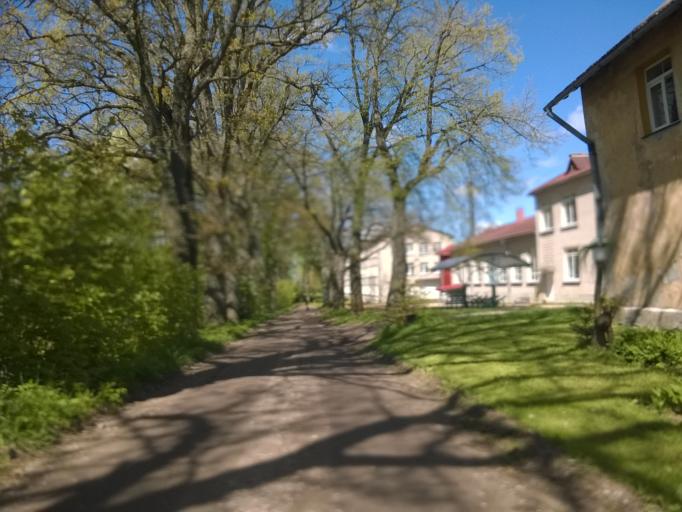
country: LV
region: Amatas Novads
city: Drabesi
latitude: 57.2443
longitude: 25.2785
